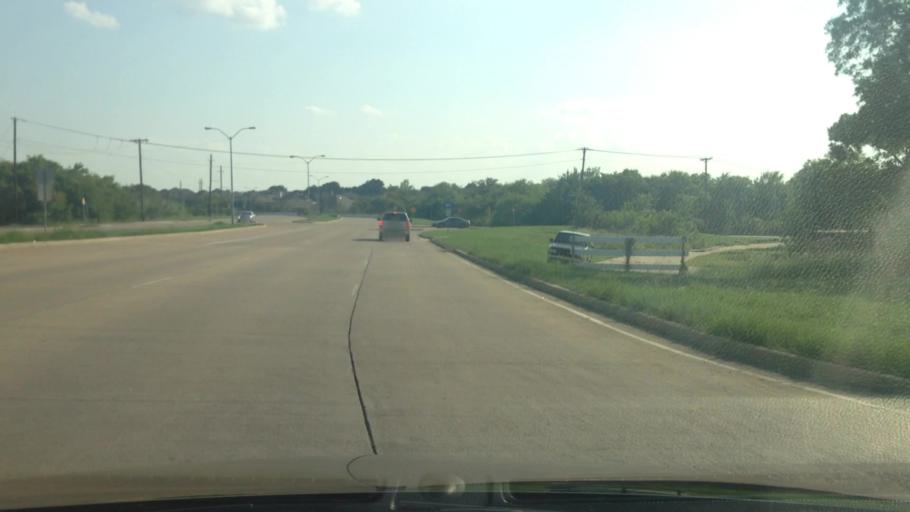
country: US
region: Texas
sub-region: Tarrant County
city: Edgecliff Village
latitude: 32.6621
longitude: -97.3322
